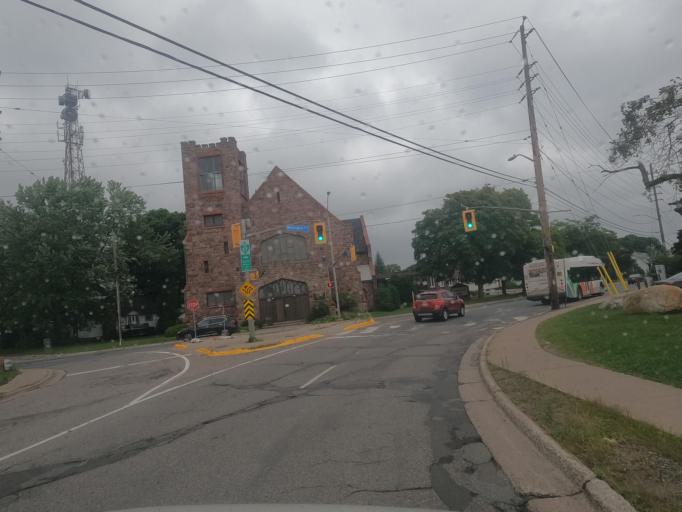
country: CA
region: Ontario
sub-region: Algoma
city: Sault Ste. Marie
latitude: 46.5093
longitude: -84.3255
